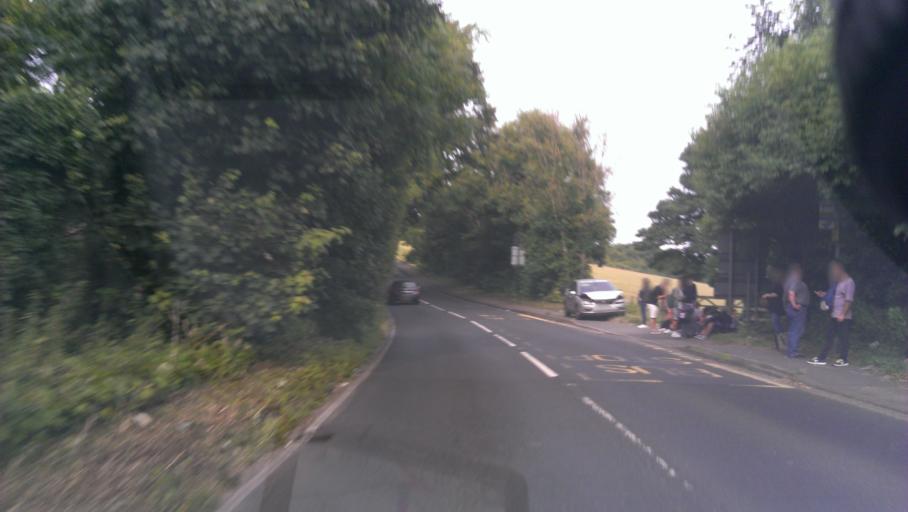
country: GB
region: England
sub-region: Kent
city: Dover
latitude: 51.1324
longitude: 1.3192
